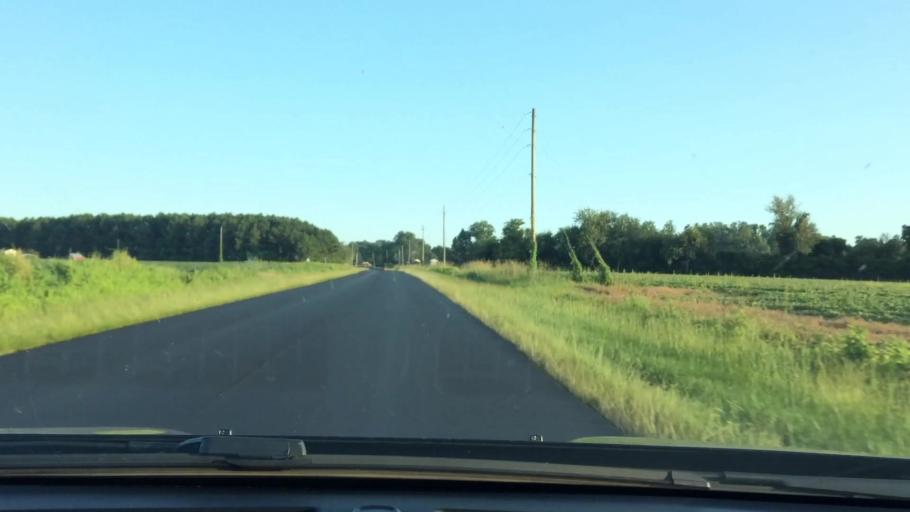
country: US
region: North Carolina
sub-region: Pitt County
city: Ayden
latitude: 35.4335
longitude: -77.4508
